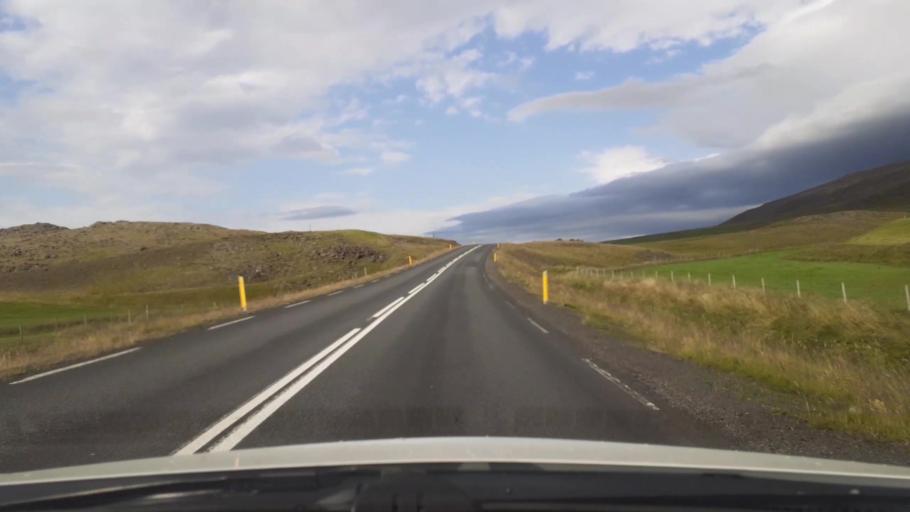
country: IS
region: Capital Region
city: Mosfellsbaer
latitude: 64.3974
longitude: -21.5157
